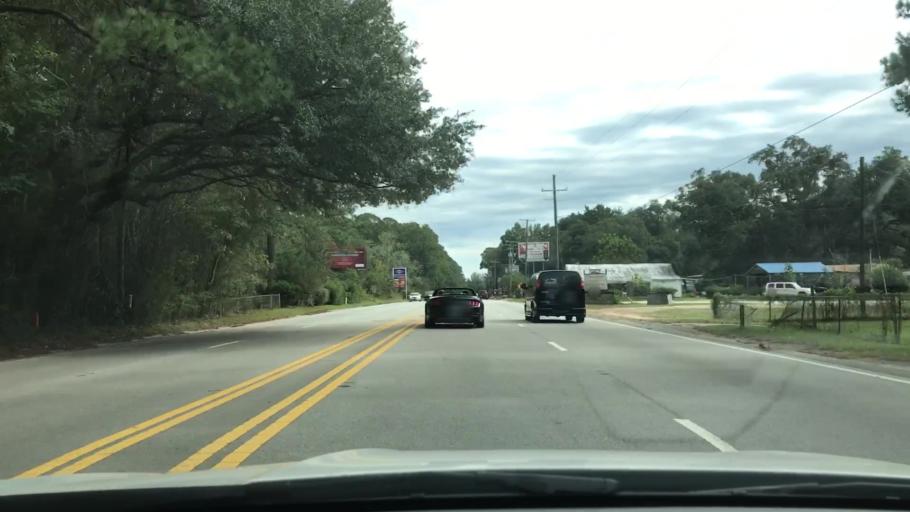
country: US
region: South Carolina
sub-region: Charleston County
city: Ravenel
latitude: 32.7715
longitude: -80.4564
